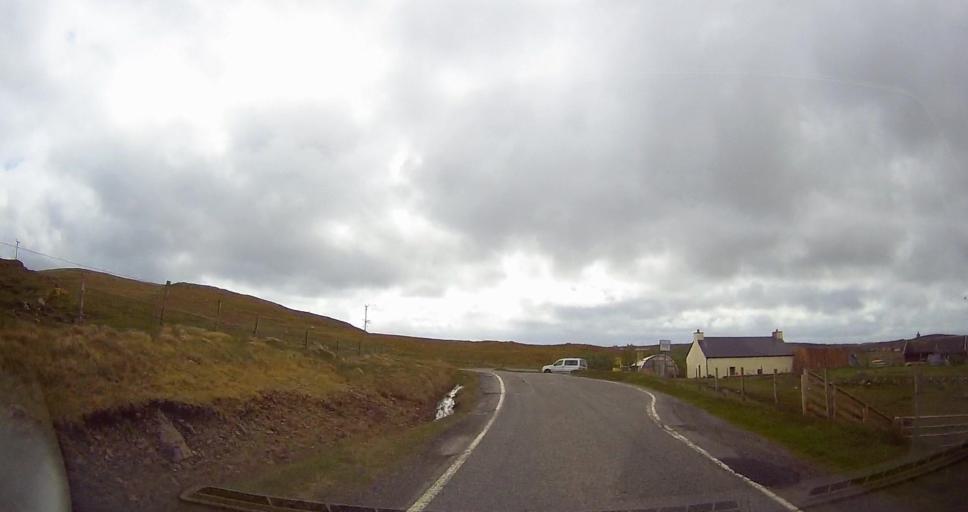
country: GB
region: Scotland
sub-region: Shetland Islands
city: Sandwick
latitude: 60.2340
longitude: -1.5511
